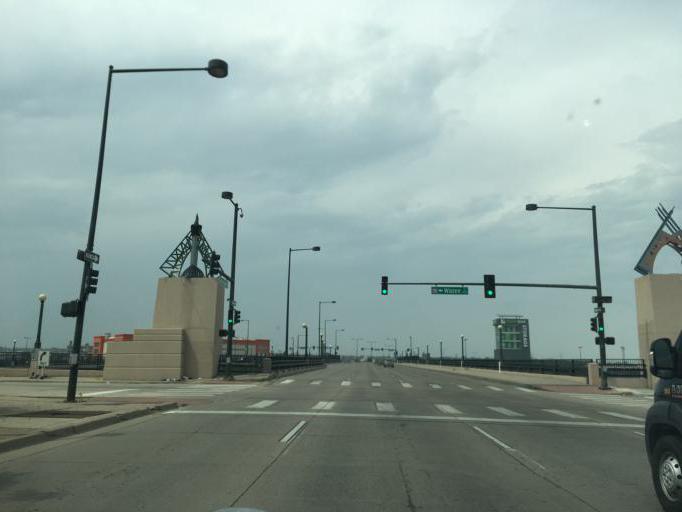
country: US
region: Colorado
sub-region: Denver County
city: Denver
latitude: 39.7576
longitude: -104.9916
